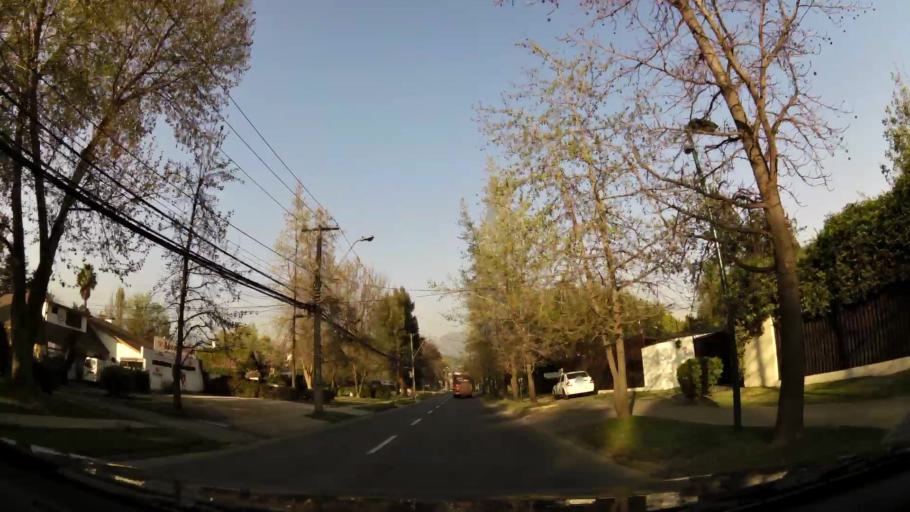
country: CL
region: Santiago Metropolitan
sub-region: Provincia de Santiago
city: Villa Presidente Frei, Nunoa, Santiago, Chile
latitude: -33.3523
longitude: -70.5153
